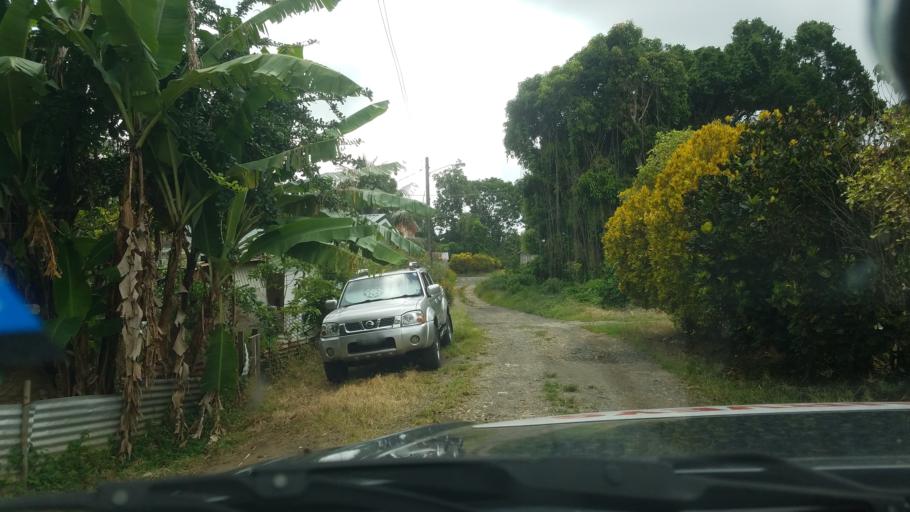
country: LC
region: Castries Quarter
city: Bisee
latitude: 14.0031
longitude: -60.9501
